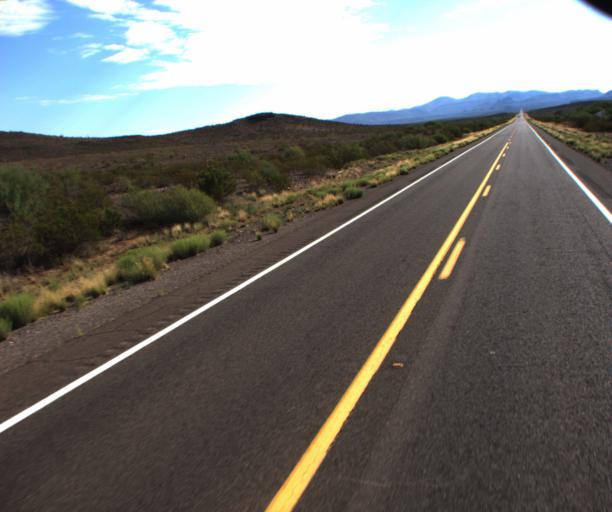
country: US
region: Arizona
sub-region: Graham County
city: Safford
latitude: 32.8038
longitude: -109.5195
